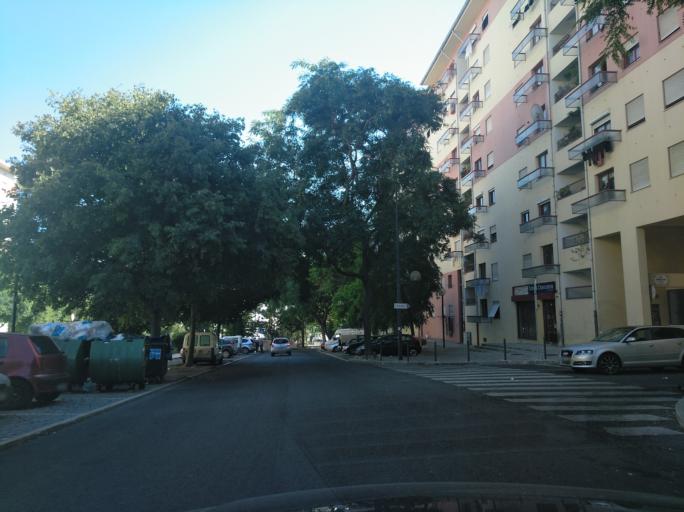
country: PT
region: Lisbon
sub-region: Lisbon
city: Lisbon
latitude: 38.7447
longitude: -9.1193
